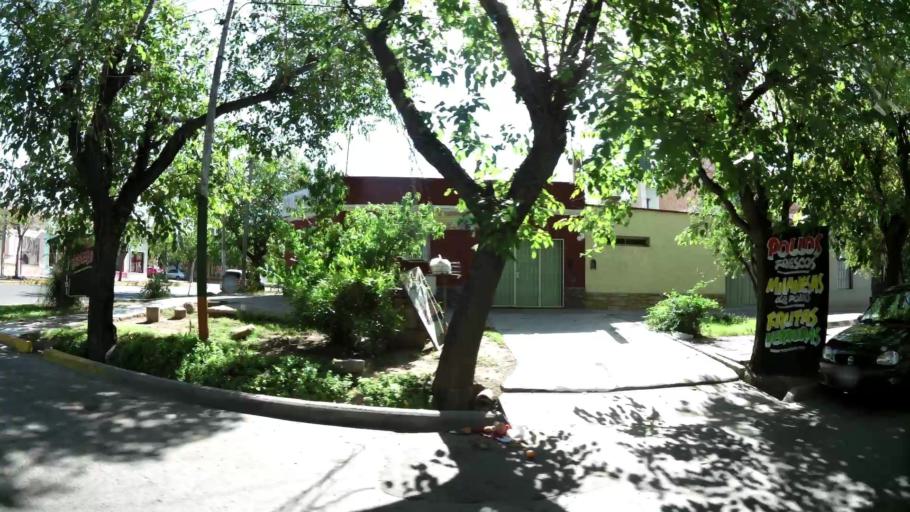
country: AR
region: Mendoza
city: Villa Nueva
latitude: -32.9044
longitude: -68.7892
